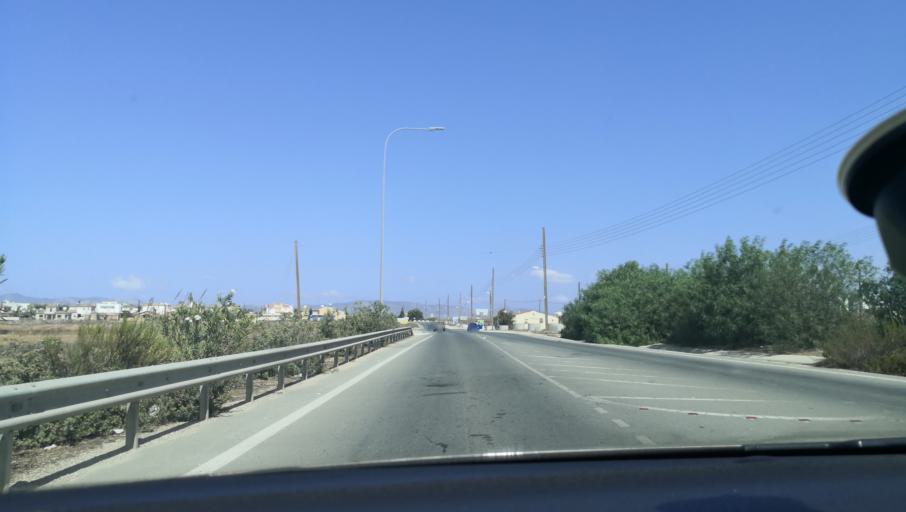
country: CY
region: Lefkosia
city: Kokkinotrimithia
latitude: 35.1630
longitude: 33.2016
